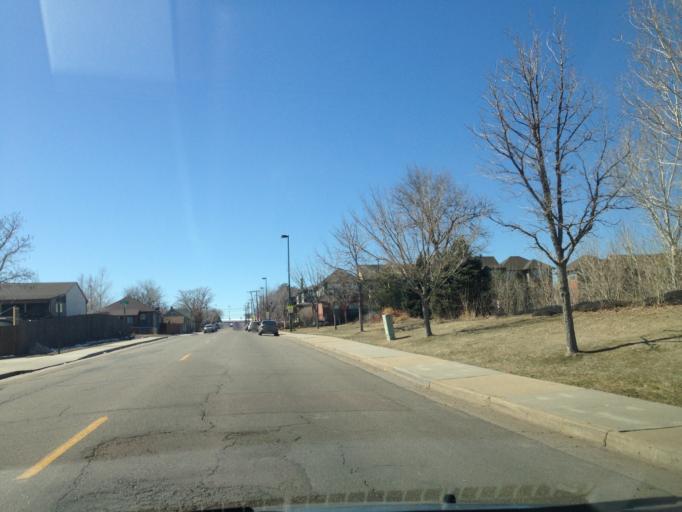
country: US
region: Colorado
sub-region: Adams County
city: Twin Lakes
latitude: 39.7893
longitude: -104.9830
